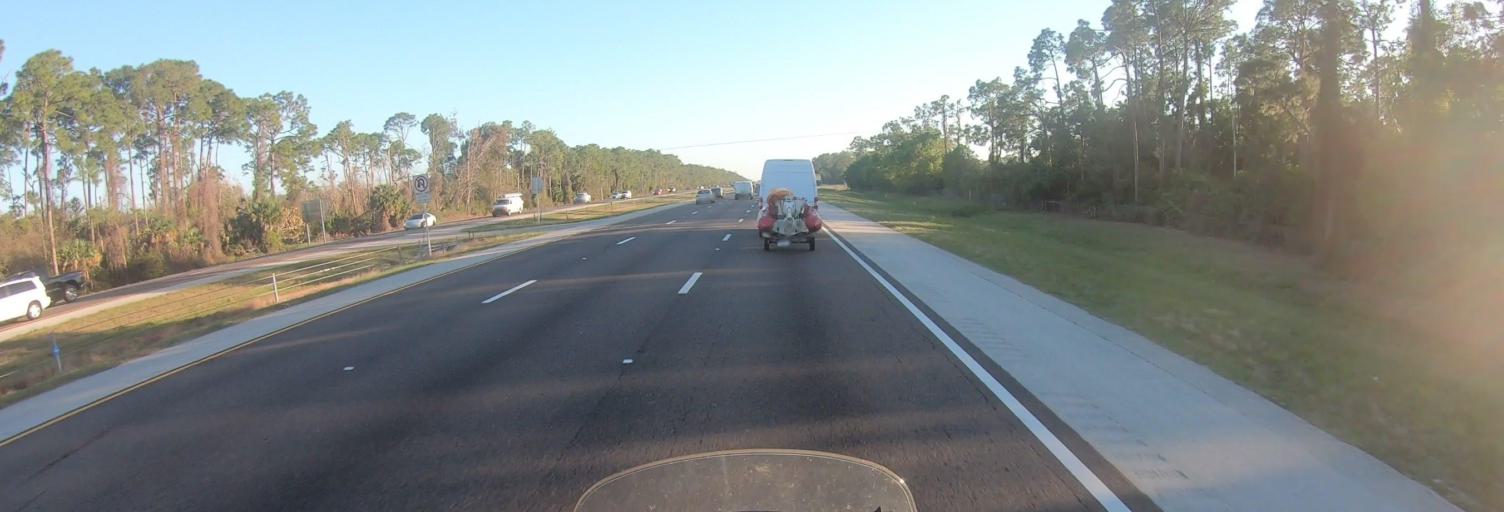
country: US
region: Florida
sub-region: Collier County
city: Vineyards
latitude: 26.2330
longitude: -81.7369
